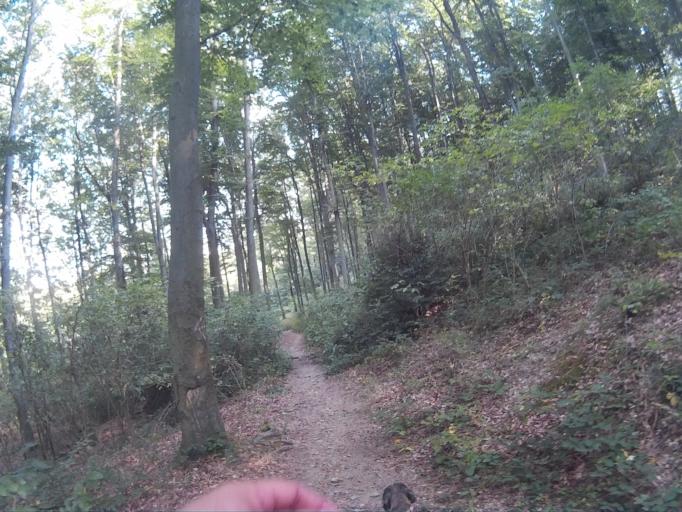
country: HU
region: Vas
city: Koszeg
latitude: 47.3996
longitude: 16.5231
